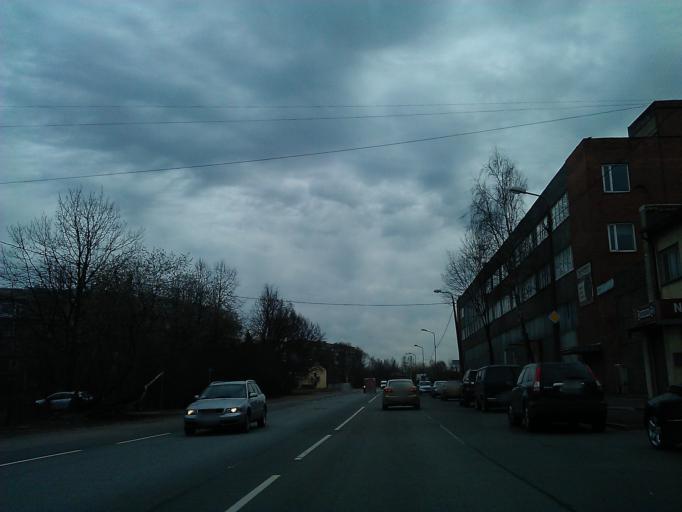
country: LV
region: Riga
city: Riga
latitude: 56.9590
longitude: 24.1655
